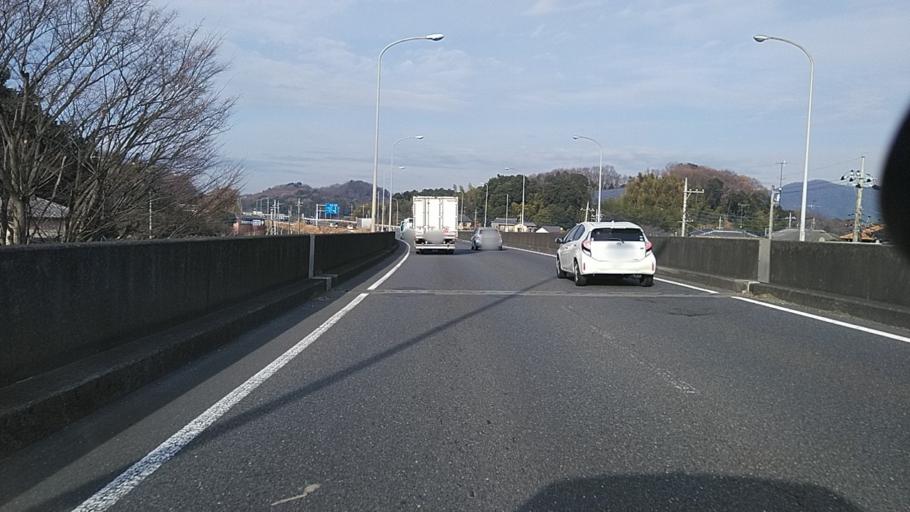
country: JP
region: Tochigi
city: Fujioka
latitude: 36.3120
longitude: 139.6790
